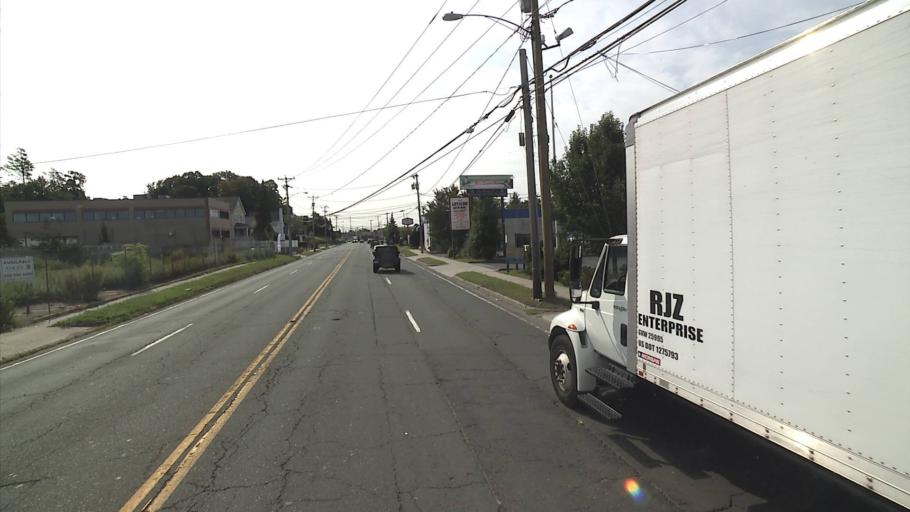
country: US
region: Connecticut
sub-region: Fairfield County
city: Norwalk
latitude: 41.1330
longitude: -73.4242
